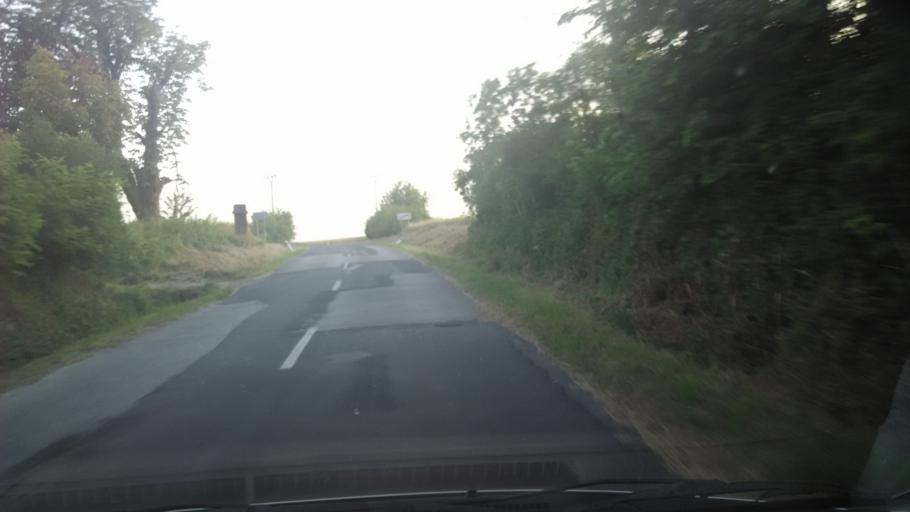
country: SK
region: Nitriansky
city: Levice
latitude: 48.1272
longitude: 18.4584
